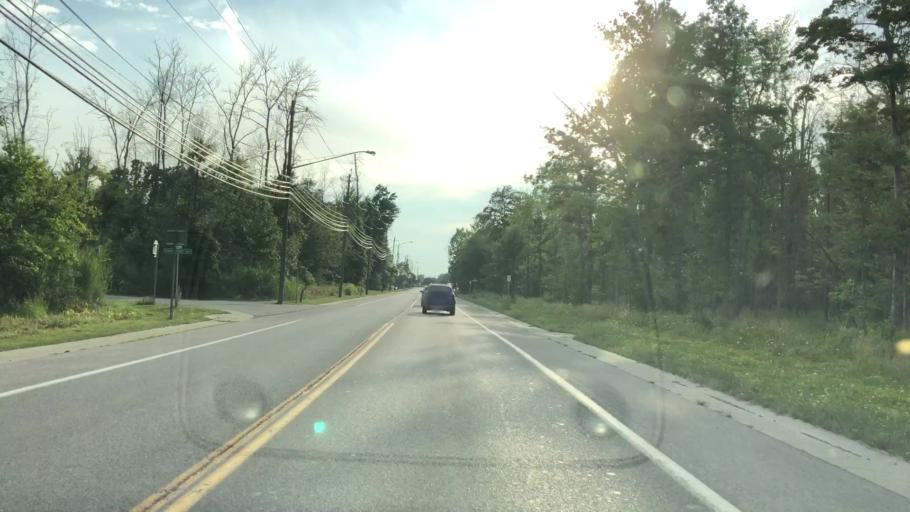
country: US
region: New York
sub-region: Erie County
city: Cheektowaga
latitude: 42.8931
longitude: -78.7463
